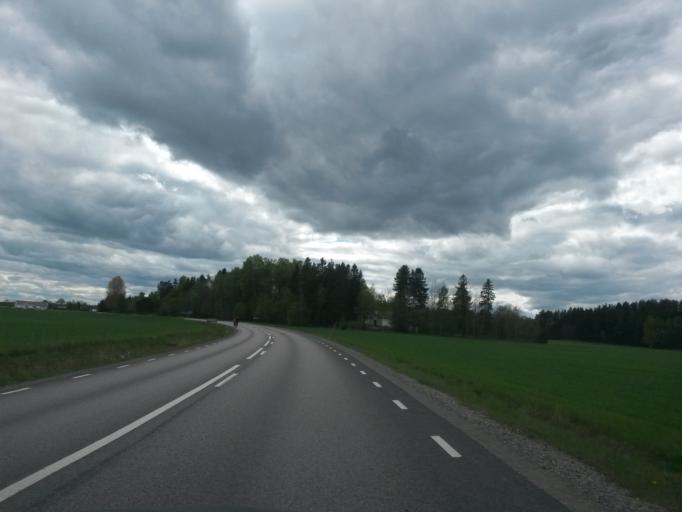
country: SE
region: Vaestra Goetaland
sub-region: Grastorps Kommun
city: Graestorp
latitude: 58.3215
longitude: 12.6773
